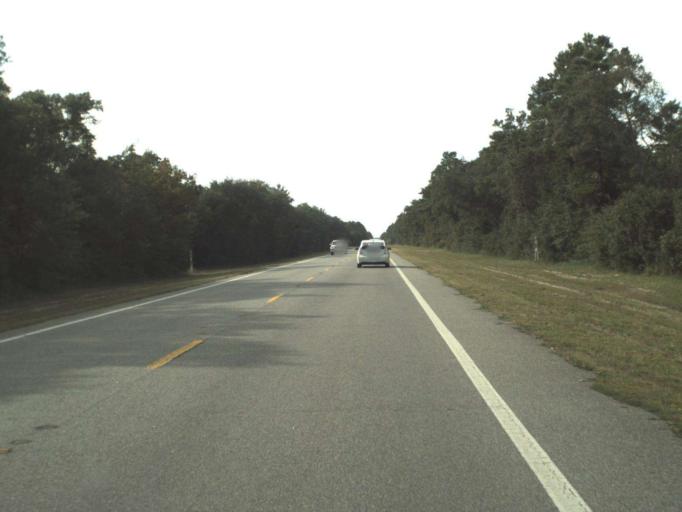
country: US
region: Florida
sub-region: Bay County
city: Mexico Beach
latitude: 29.9629
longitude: -85.4434
